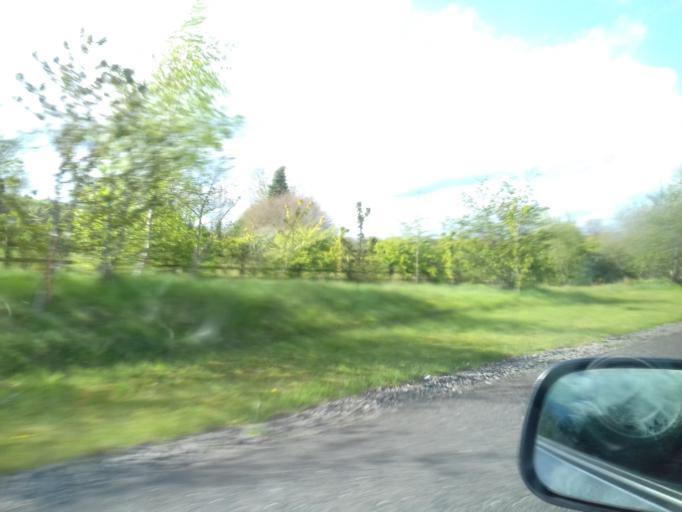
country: IE
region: Leinster
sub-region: Kildare
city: Monasterevin
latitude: 53.1233
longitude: -7.0400
